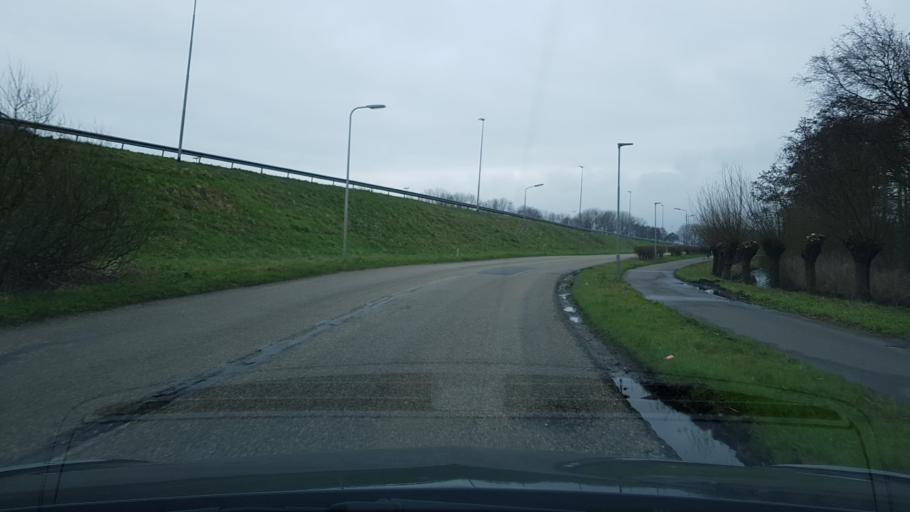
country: NL
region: North Holland
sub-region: Gemeente Haarlem
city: Haarlem
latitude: 52.3837
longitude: 4.7096
